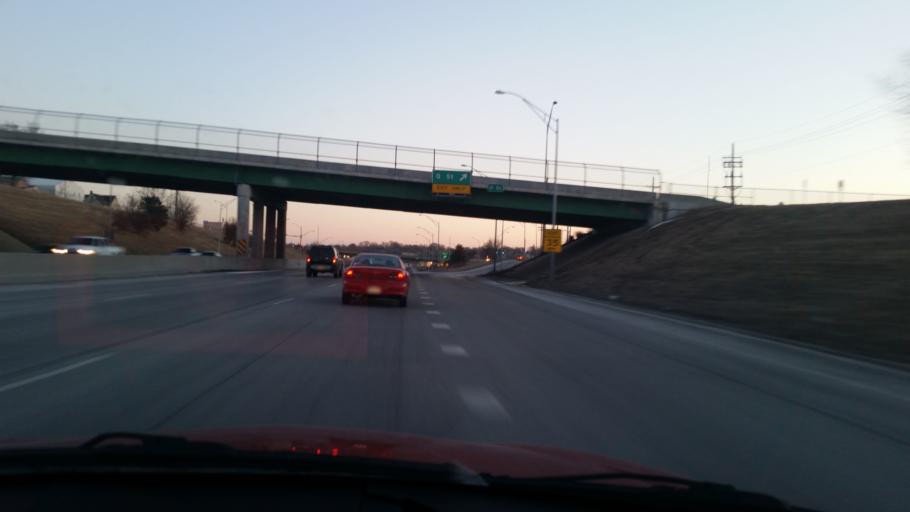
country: US
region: Nebraska
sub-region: Douglas County
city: Omaha
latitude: 41.2089
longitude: -95.9494
